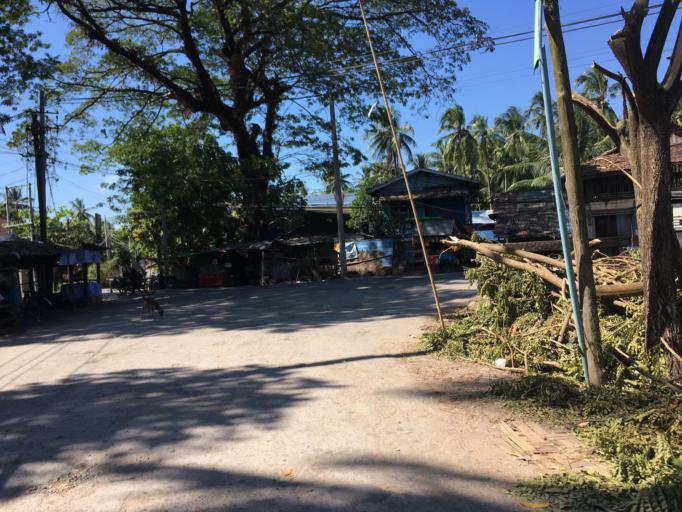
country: MM
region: Mon
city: Mawlamyine
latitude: 16.4546
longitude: 97.6279
